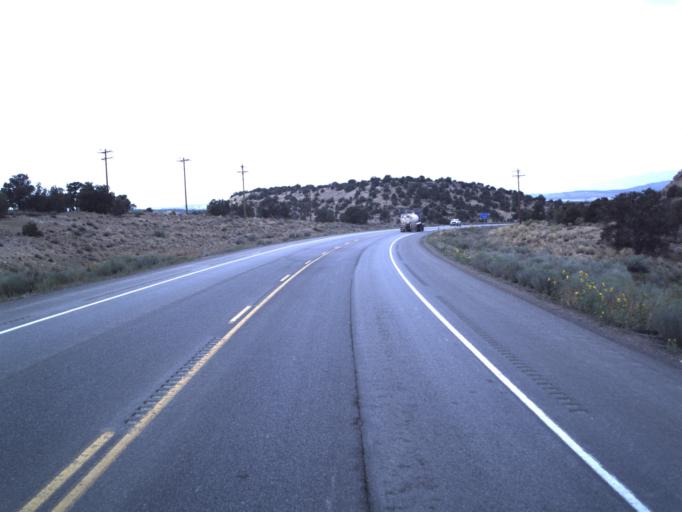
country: US
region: Utah
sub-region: Duchesne County
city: Duchesne
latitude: 40.1664
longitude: -110.4801
